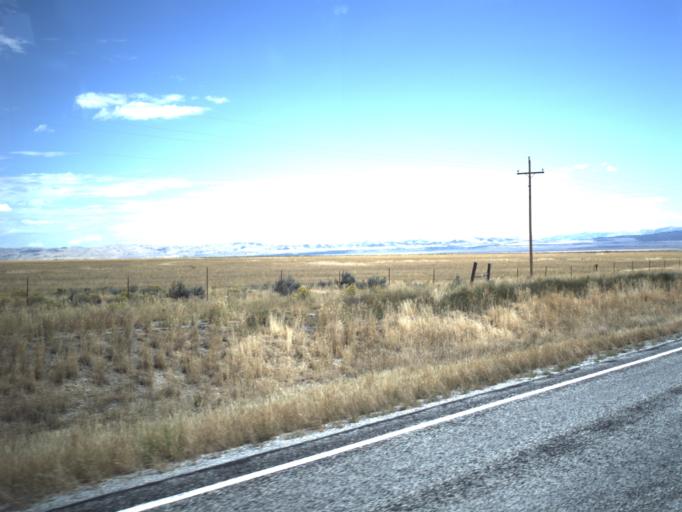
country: US
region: Idaho
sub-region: Oneida County
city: Malad City
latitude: 41.9654
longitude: -113.0364
